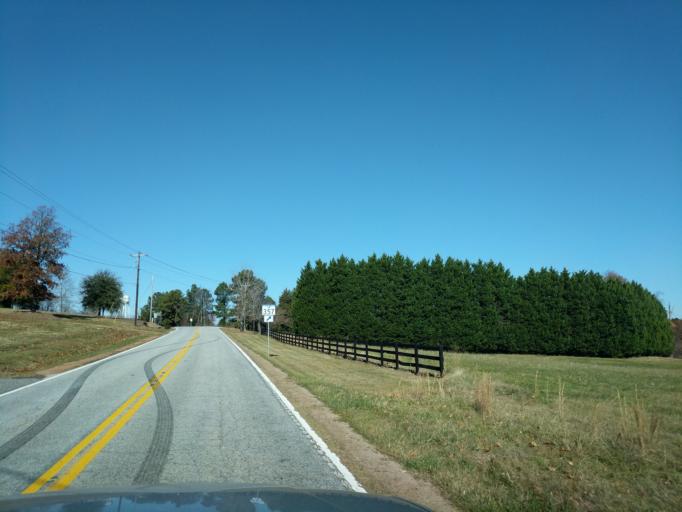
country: US
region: South Carolina
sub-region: Spartanburg County
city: Inman Mills
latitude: 35.0565
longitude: -82.1796
